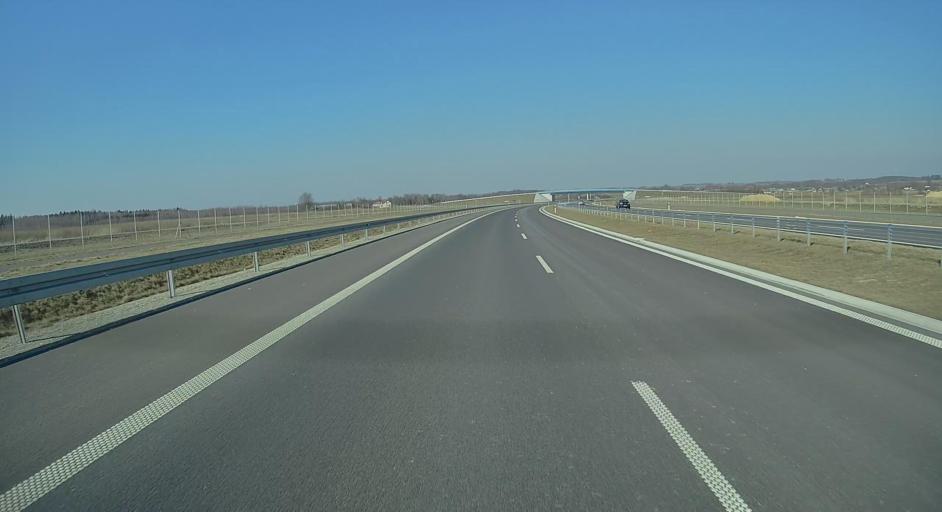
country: PL
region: Lublin Voivodeship
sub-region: Powiat janowski
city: Modliborzyce
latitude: 50.7442
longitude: 22.3024
